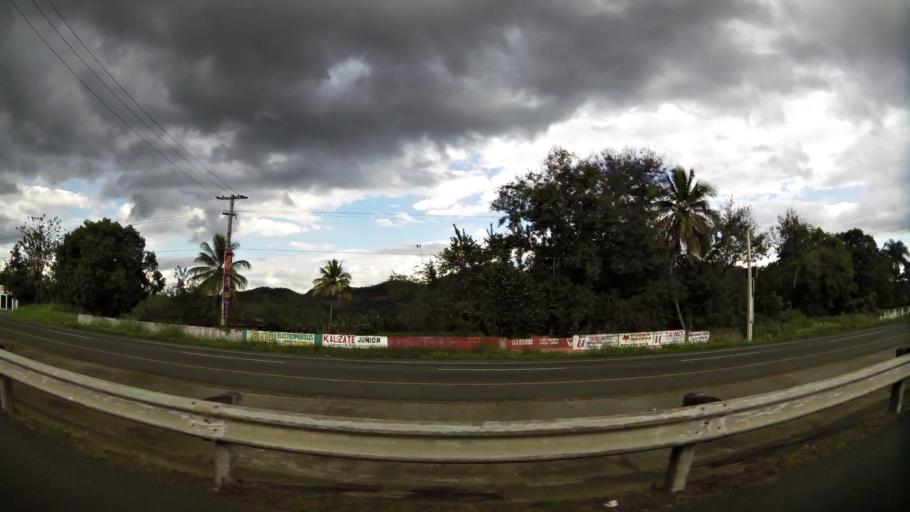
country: DO
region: Monsenor Nouel
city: Bonao
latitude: 18.9827
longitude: -70.4270
